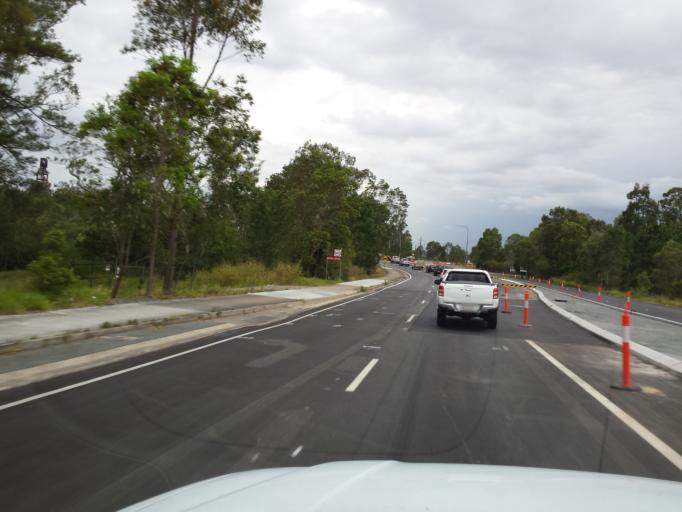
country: AU
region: Queensland
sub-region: Gold Coast
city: Oxenford
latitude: -27.8590
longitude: 153.3113
